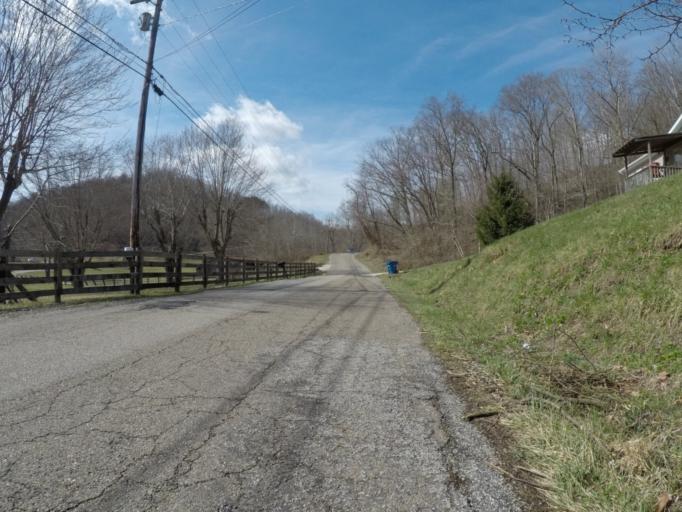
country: US
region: West Virginia
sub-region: Cabell County
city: Huntington
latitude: 38.4788
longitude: -82.4984
